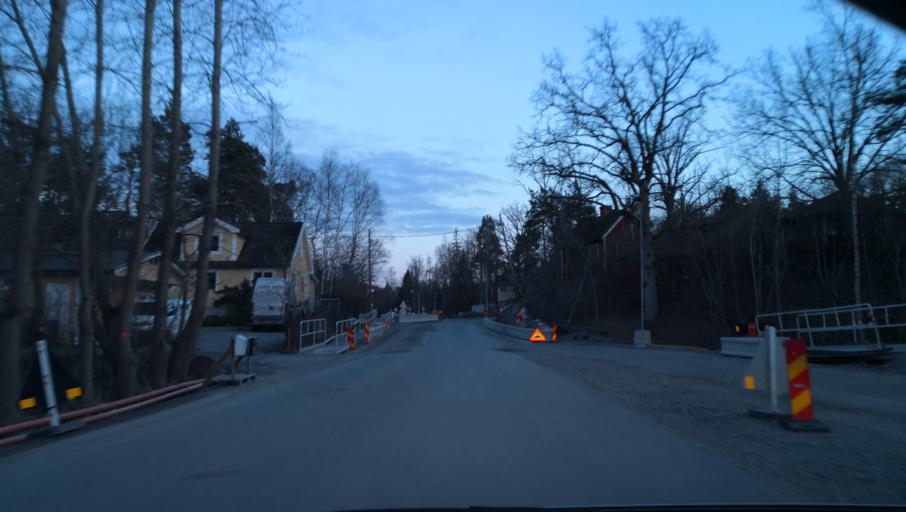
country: SE
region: Stockholm
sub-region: Nacka Kommun
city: Kummelnas
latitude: 59.3442
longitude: 18.2913
